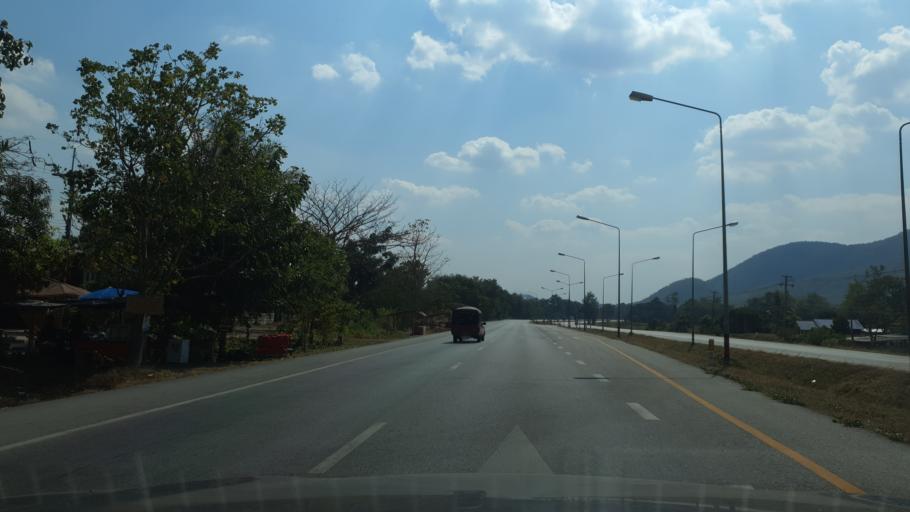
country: TH
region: Lampang
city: Mae Phrik
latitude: 17.3558
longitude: 99.1488
